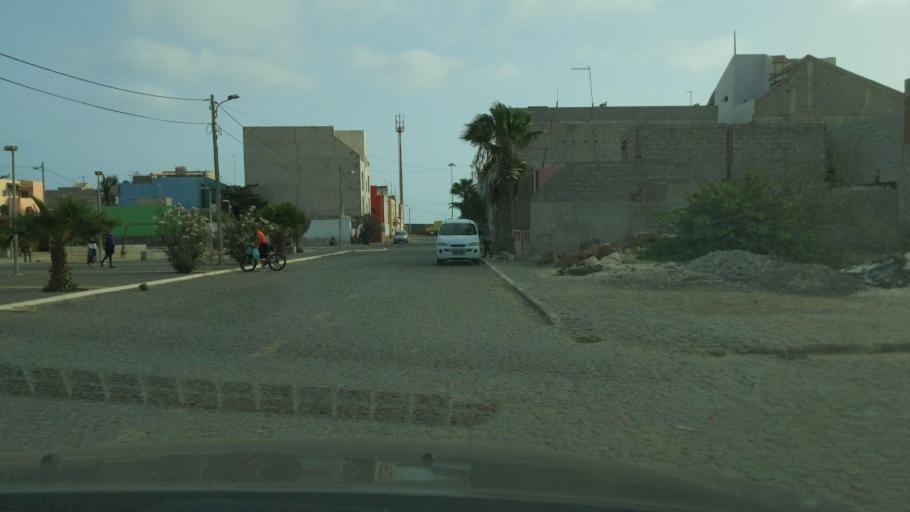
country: CV
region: Sal
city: Espargos
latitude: 16.7597
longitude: -22.9816
